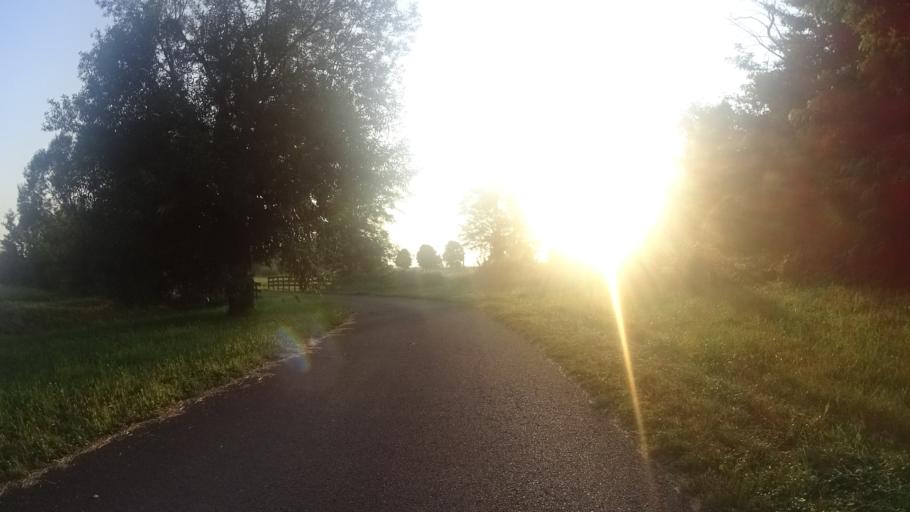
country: HU
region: Zala
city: Zalakomar
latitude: 46.5318
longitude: 17.1249
